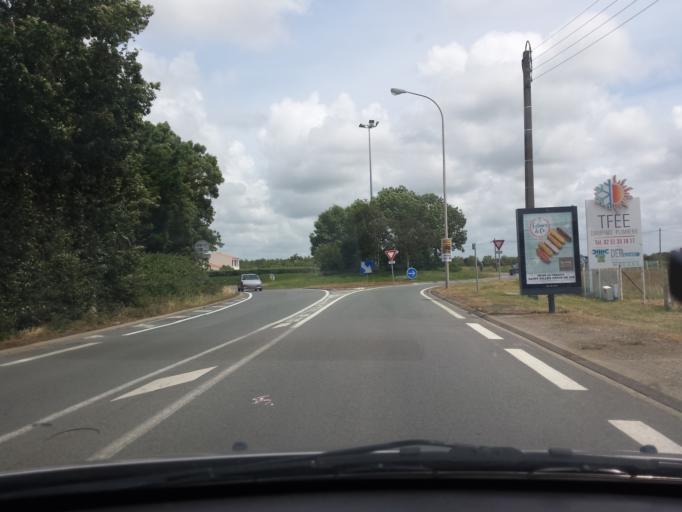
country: FR
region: Pays de la Loire
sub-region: Departement de la Vendee
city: Le Fenouiller
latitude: 46.6934
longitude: -1.8989
